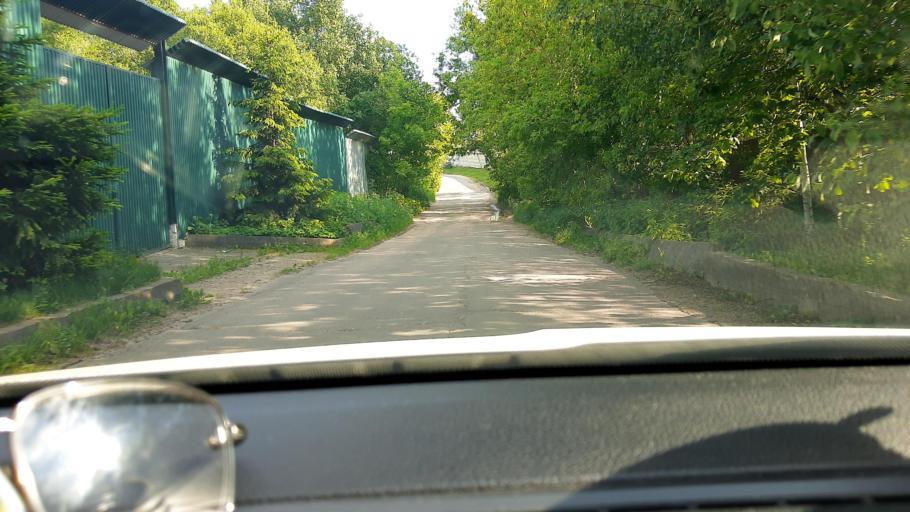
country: RU
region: Moscow
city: Novo-Peredelkino
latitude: 55.6716
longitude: 37.3196
